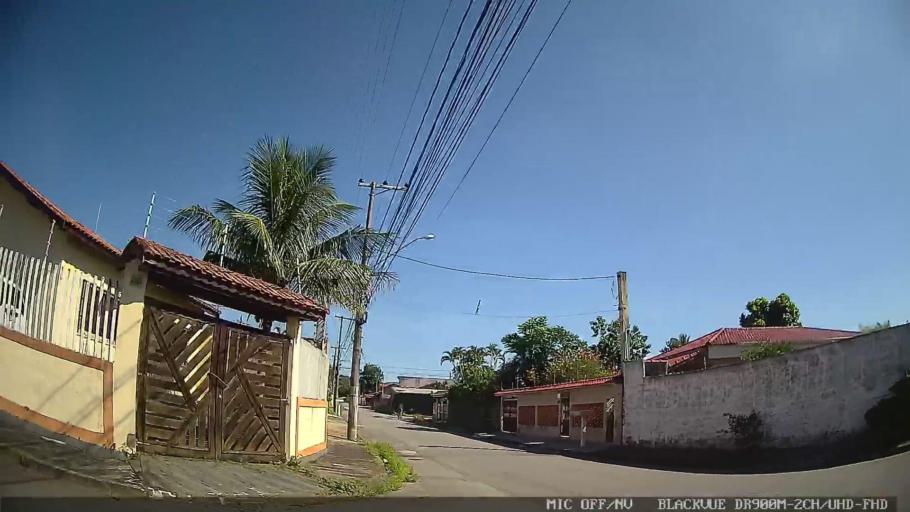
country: BR
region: Sao Paulo
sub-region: Peruibe
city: Peruibe
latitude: -24.2754
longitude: -46.9441
